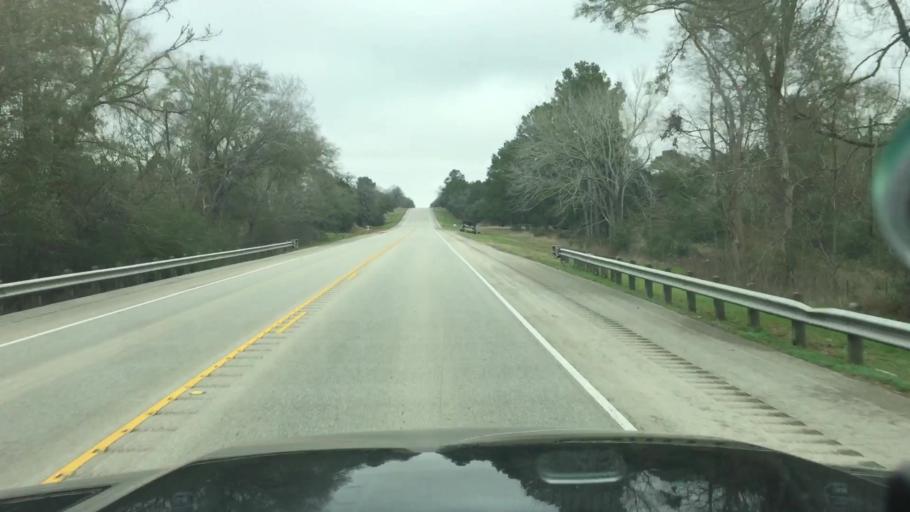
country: US
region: Texas
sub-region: Lee County
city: Giddings
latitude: 30.0684
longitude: -96.9166
